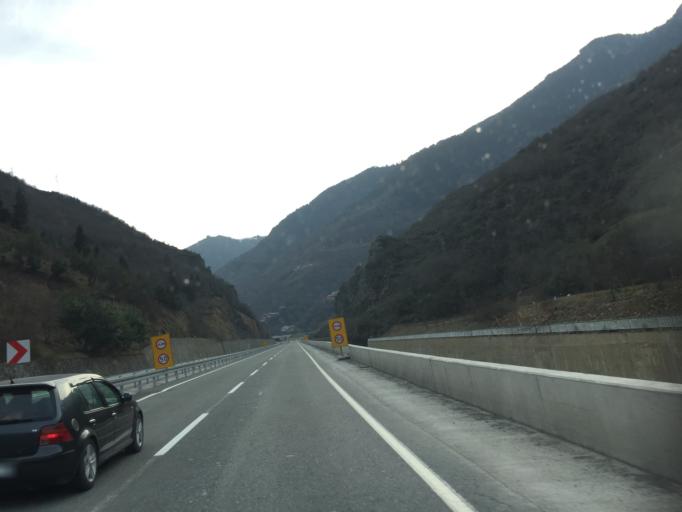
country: TR
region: Trabzon
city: Macka
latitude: 40.7854
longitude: 39.5764
